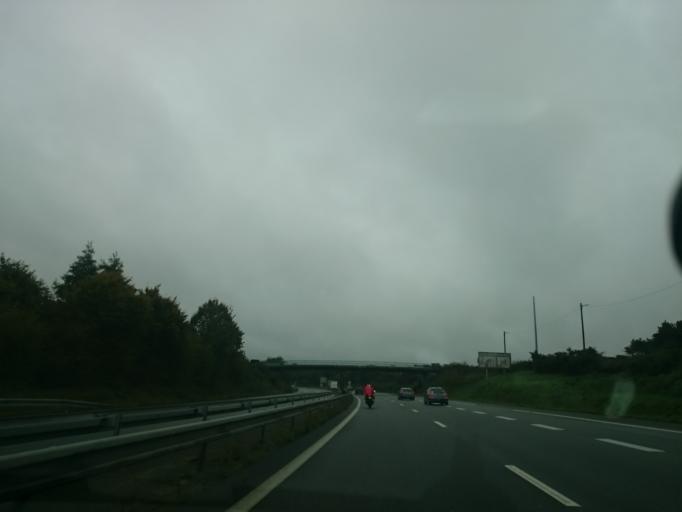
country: FR
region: Brittany
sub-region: Departement du Morbihan
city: Auray
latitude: 47.6604
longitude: -3.0069
